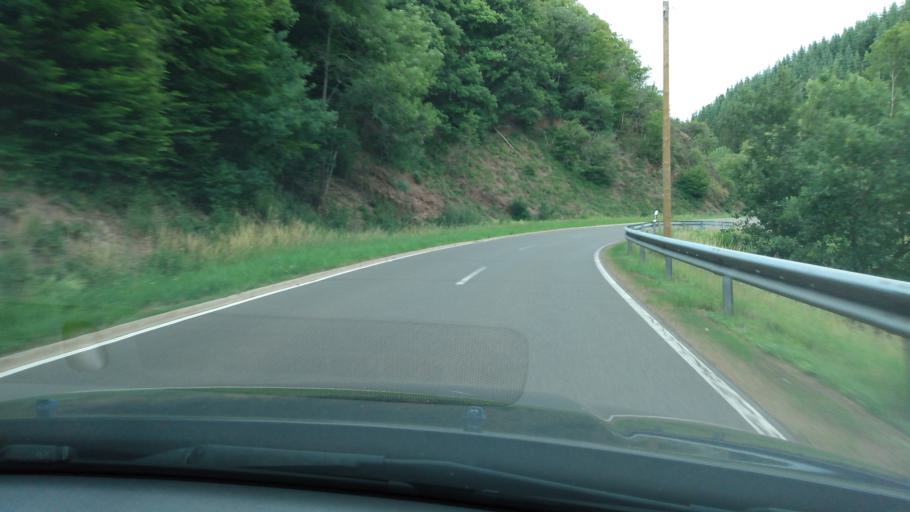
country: DE
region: Rheinland-Pfalz
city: Bettenfeld
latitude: 50.0982
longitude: 6.7711
